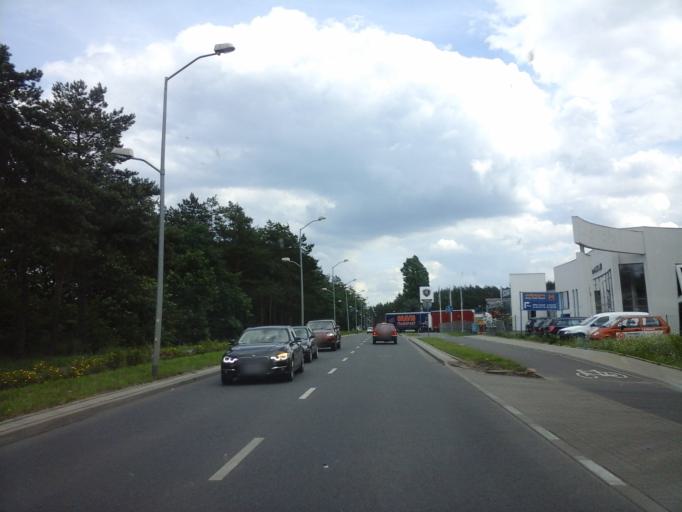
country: PL
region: West Pomeranian Voivodeship
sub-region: Szczecin
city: Szczecin
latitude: 53.3815
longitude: 14.6768
